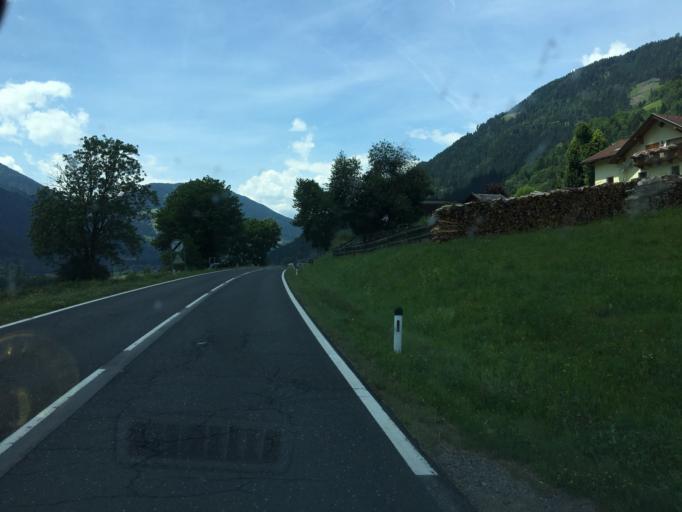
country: AT
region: Carinthia
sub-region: Politischer Bezirk Spittal an der Drau
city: Rangersdorf
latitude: 46.8609
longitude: 12.9626
